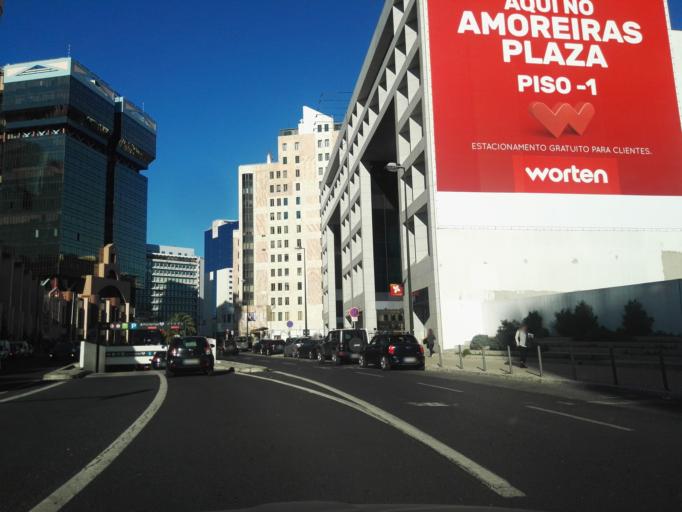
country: PT
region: Lisbon
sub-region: Lisbon
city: Lisbon
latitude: 38.7222
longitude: -9.1613
